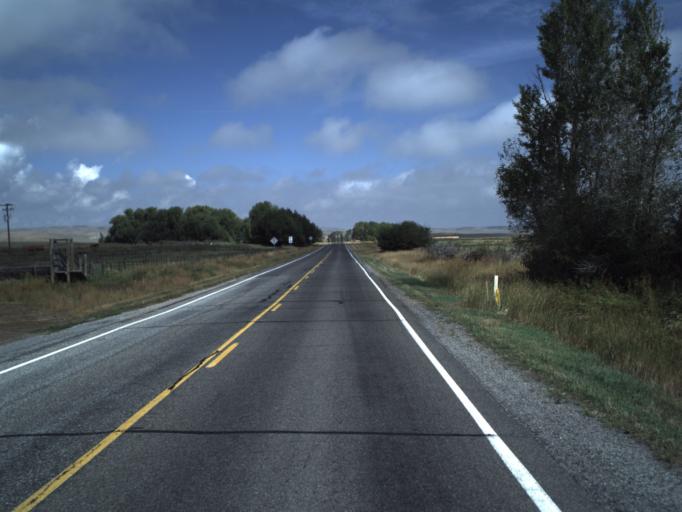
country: US
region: Utah
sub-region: Rich County
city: Randolph
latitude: 41.7070
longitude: -111.1593
